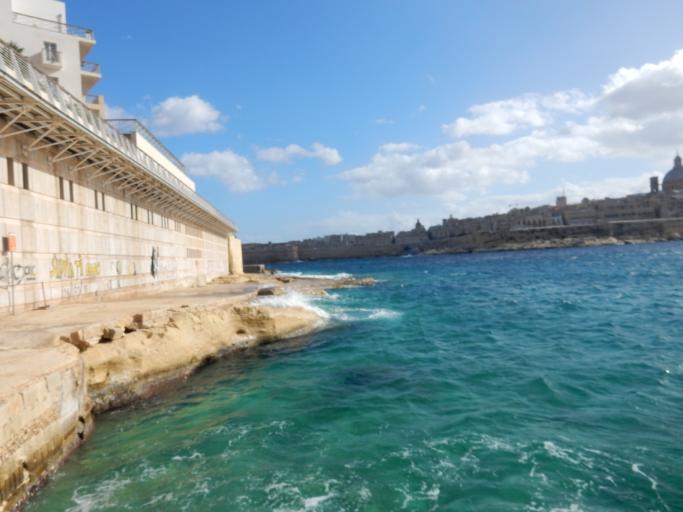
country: MT
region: Il-Belt Valletta
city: Valletta
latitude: 35.9061
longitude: 14.5108
